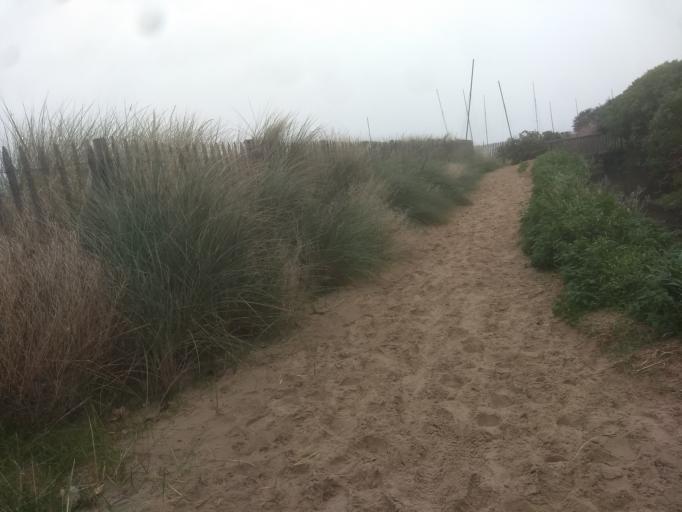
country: FR
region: Nord-Pas-de-Calais
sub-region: Departement du Pas-de-Calais
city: Wissant
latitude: 50.8869
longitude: 1.6602
